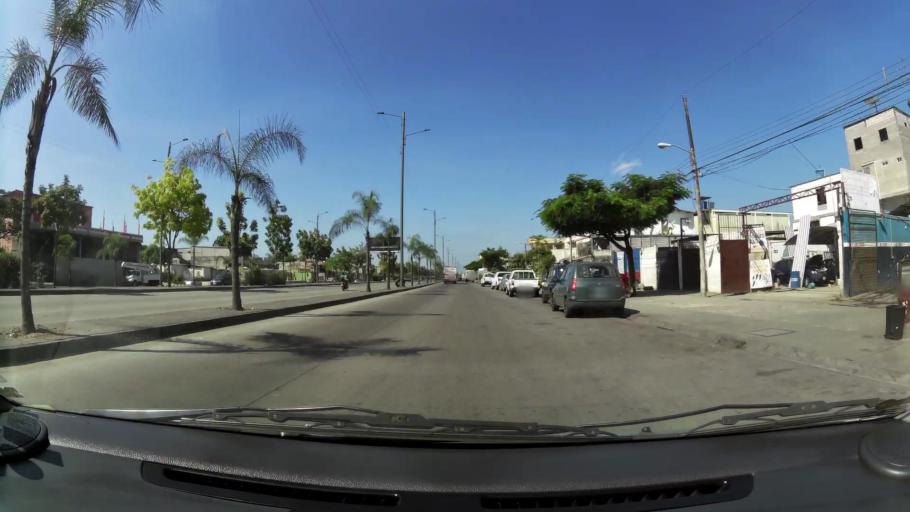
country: EC
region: Guayas
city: Eloy Alfaro
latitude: -2.1232
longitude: -79.8830
